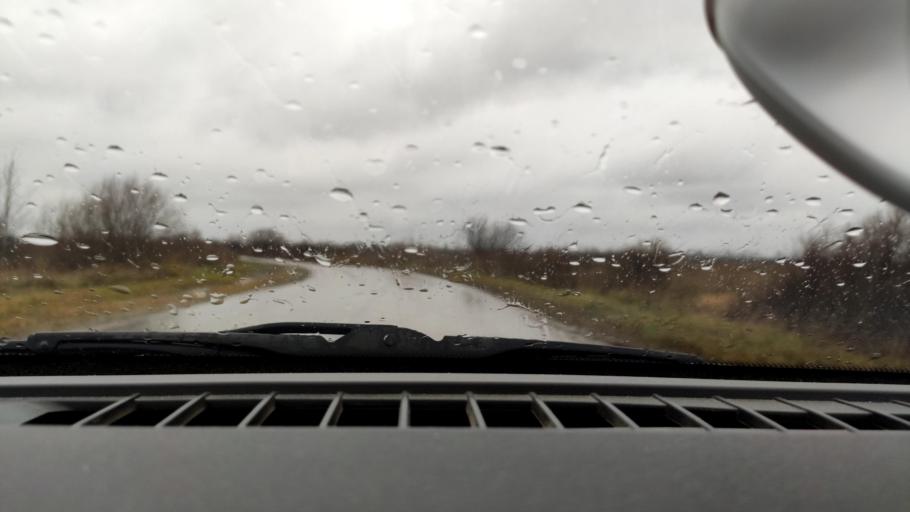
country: RU
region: Perm
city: Kondratovo
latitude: 57.9960
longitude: 56.0860
